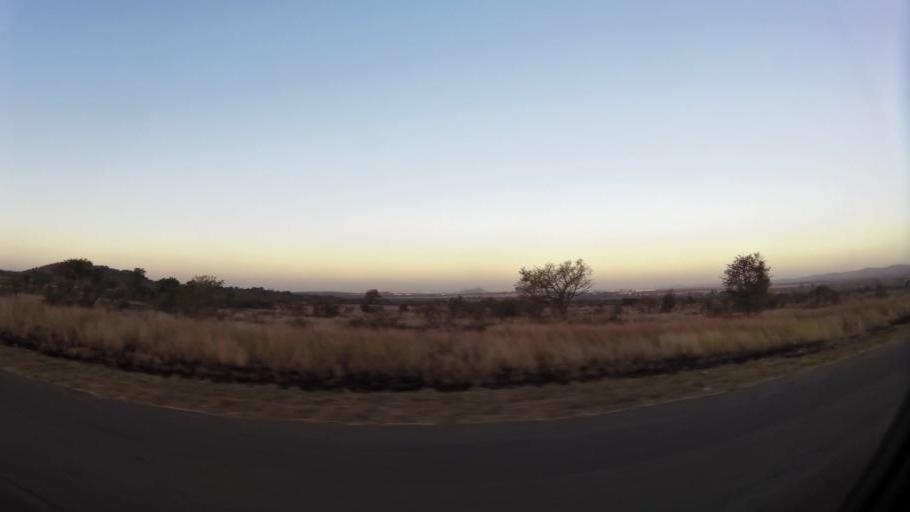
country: ZA
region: North-West
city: Ga-Rankuwa
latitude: -25.6136
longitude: 28.0389
